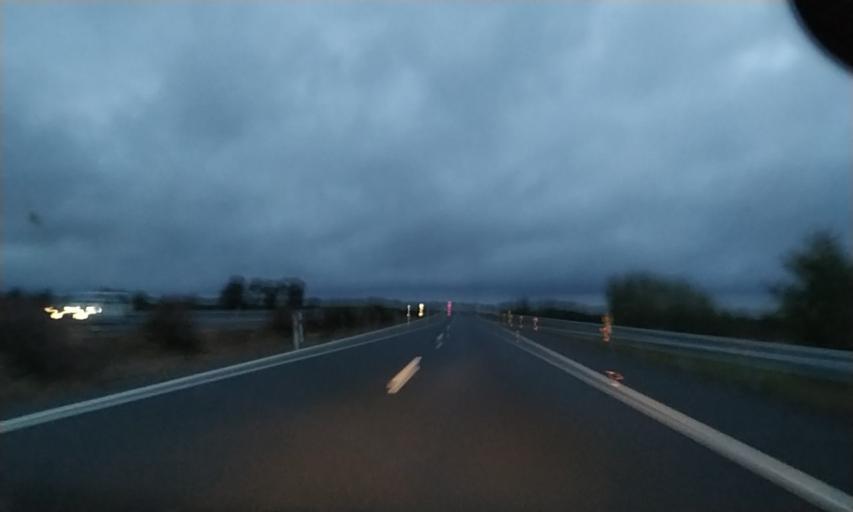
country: ES
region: Extremadura
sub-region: Provincia de Caceres
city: Aldea del Cano
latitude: 39.2590
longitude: -6.3132
